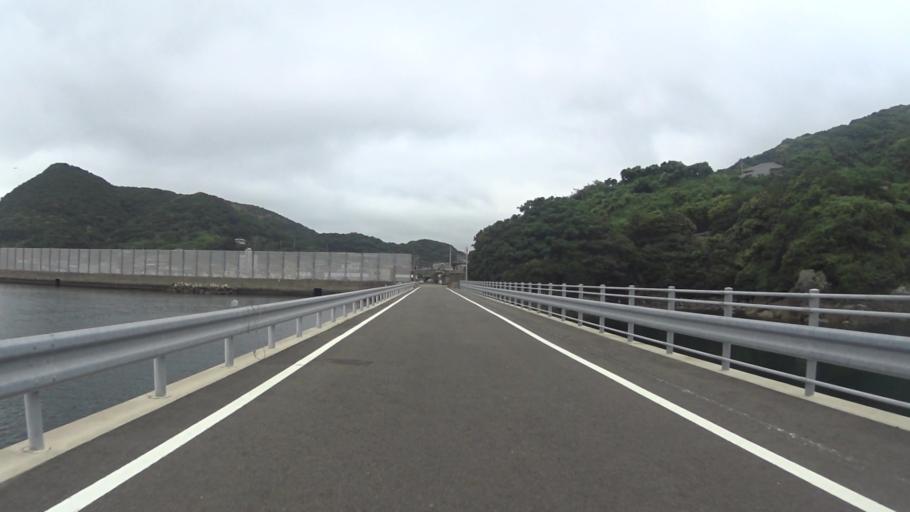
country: JP
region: Nagasaki
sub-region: Hirado Shi
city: Hirado
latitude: 33.1901
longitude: 129.3576
